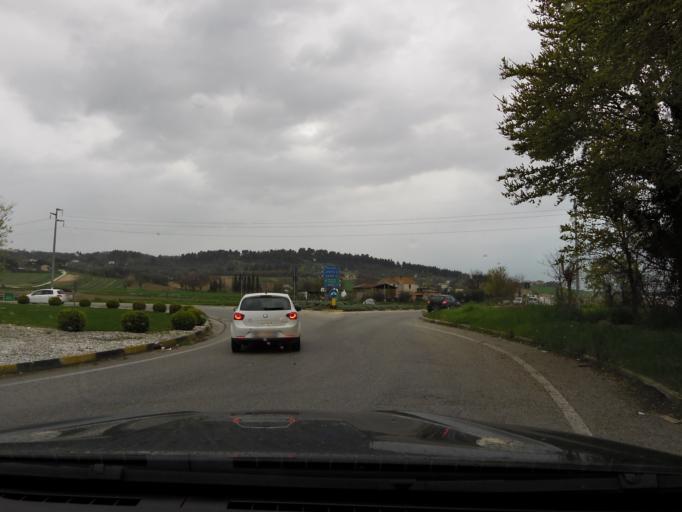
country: IT
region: The Marches
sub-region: Provincia di Ancona
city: Villa Musone
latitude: 43.4554
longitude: 13.5957
